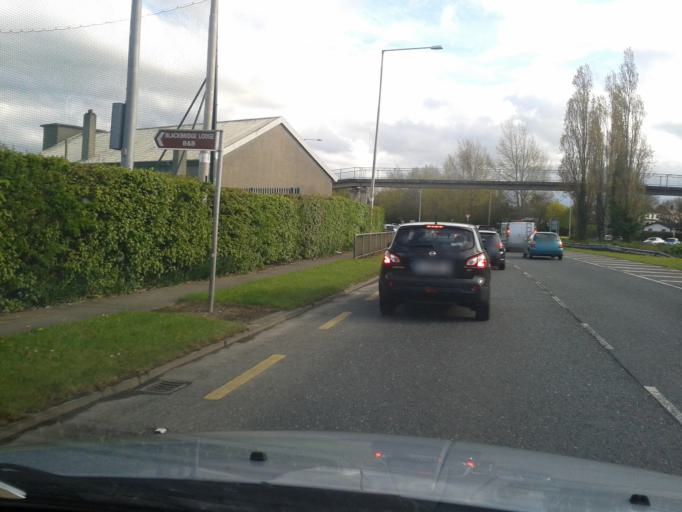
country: IE
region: Leinster
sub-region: Fingal County
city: Swords
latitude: 53.4661
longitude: -6.2146
